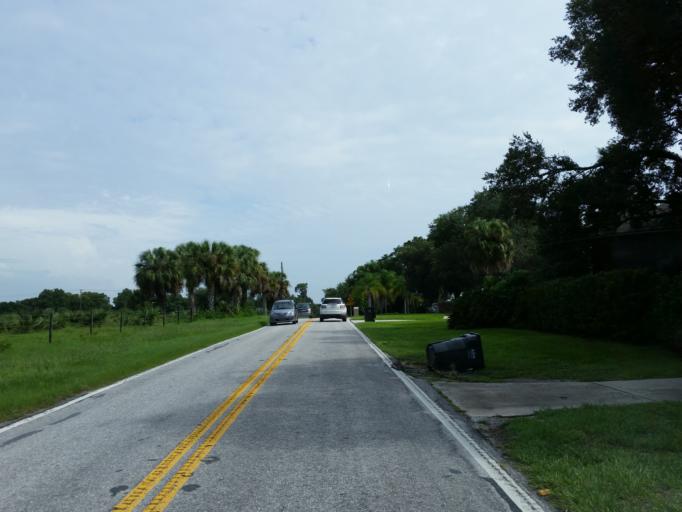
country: US
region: Florida
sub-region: Hillsborough County
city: Bloomingdale
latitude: 27.9060
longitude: -82.2528
